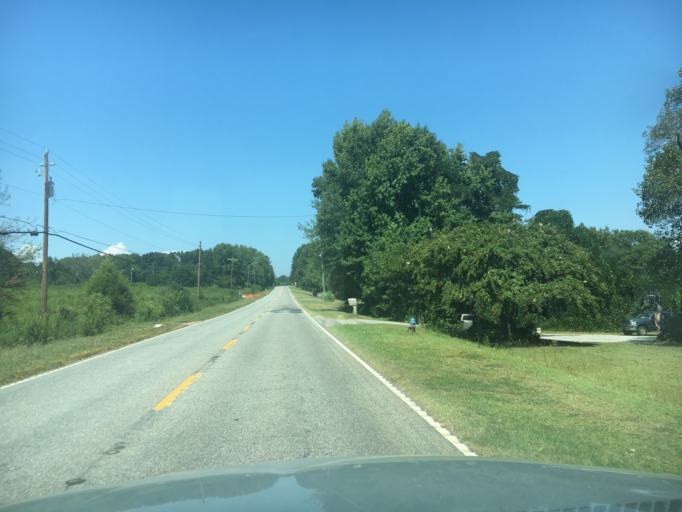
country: US
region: South Carolina
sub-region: Spartanburg County
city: Boiling Springs
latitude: 35.1262
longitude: -82.0328
